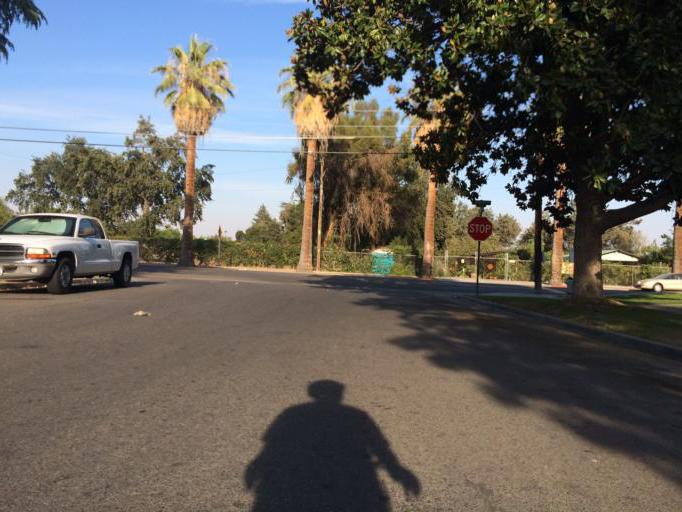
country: US
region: California
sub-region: Fresno County
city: Sunnyside
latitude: 36.7666
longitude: -119.7322
